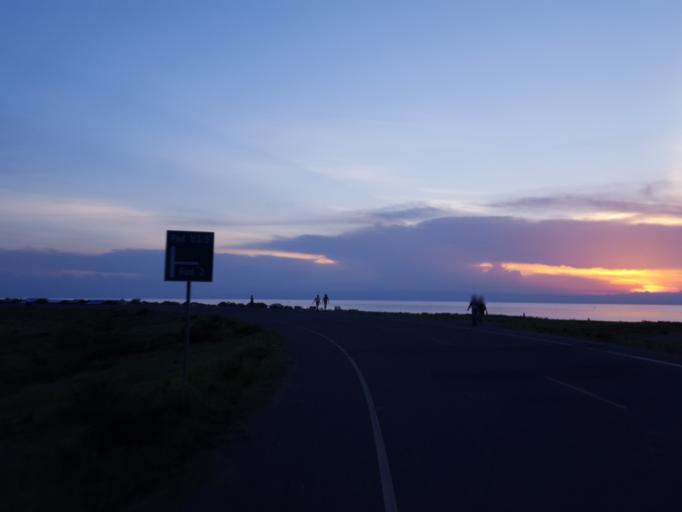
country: UG
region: Western Region
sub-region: Kibale District
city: Kagadi
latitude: 1.2534
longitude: 30.7498
